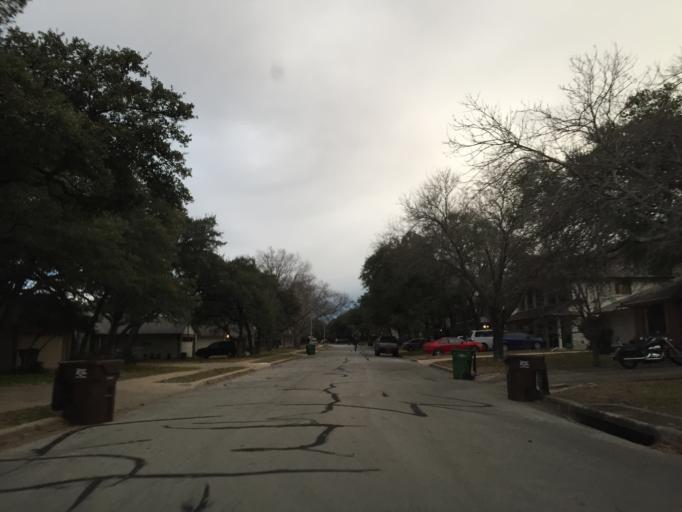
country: US
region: Texas
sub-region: Williamson County
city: Jollyville
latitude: 30.4479
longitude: -97.7517
